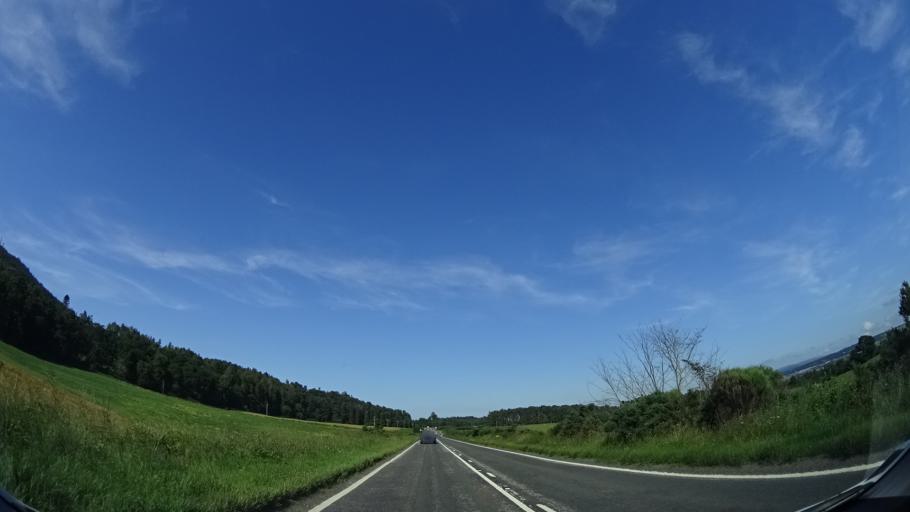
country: GB
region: Scotland
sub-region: Highland
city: Inverness
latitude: 57.4488
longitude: -4.2860
